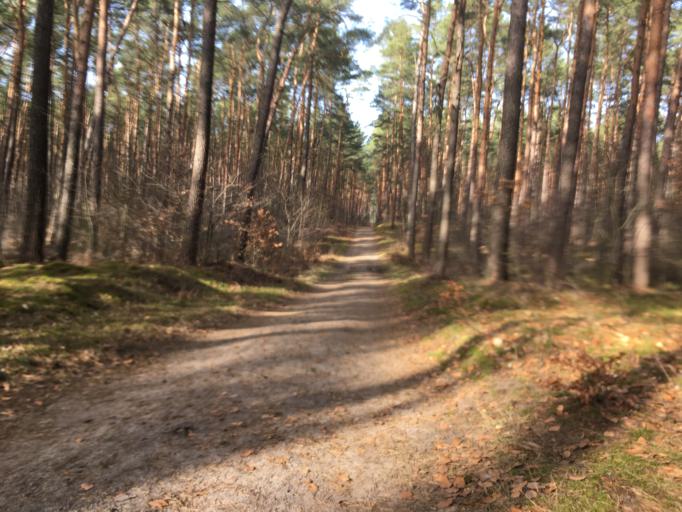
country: DE
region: Brandenburg
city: Bernau bei Berlin
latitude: 52.6990
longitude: 13.5287
